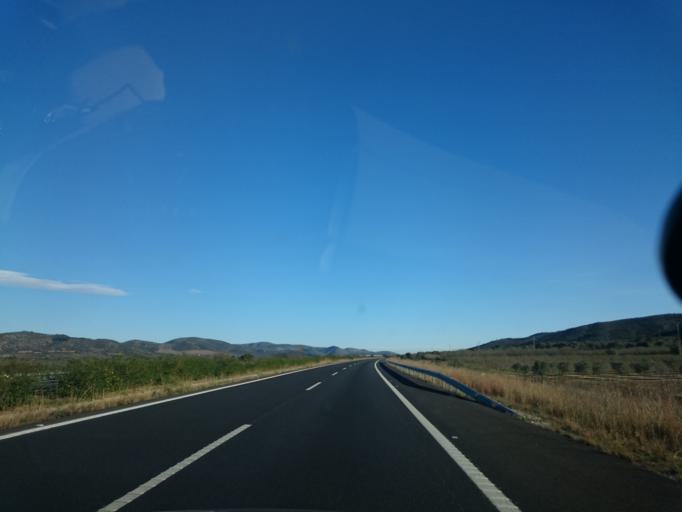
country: ES
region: Valencia
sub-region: Provincia de Castello
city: Alcala de Xivert
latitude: 40.3111
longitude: 0.2429
